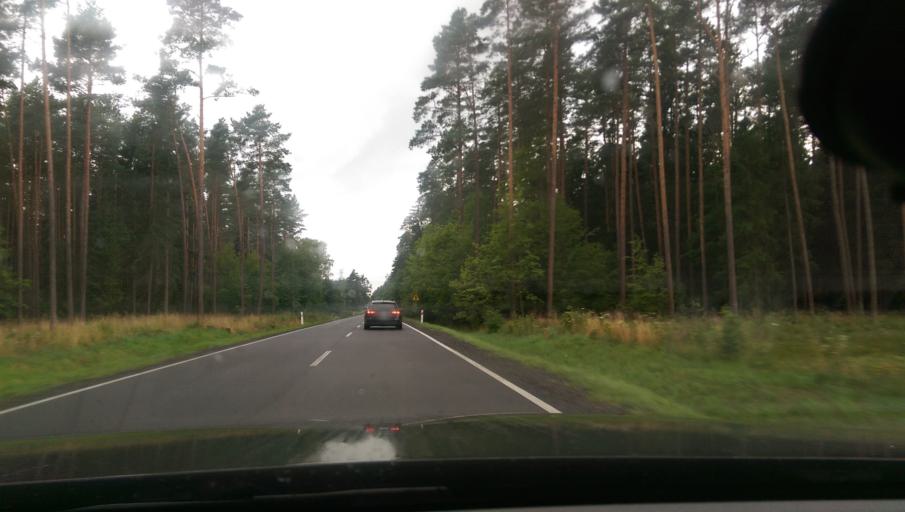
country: PL
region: Warmian-Masurian Voivodeship
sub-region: Powiat szczycienski
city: Szczytno
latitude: 53.5614
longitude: 21.0579
